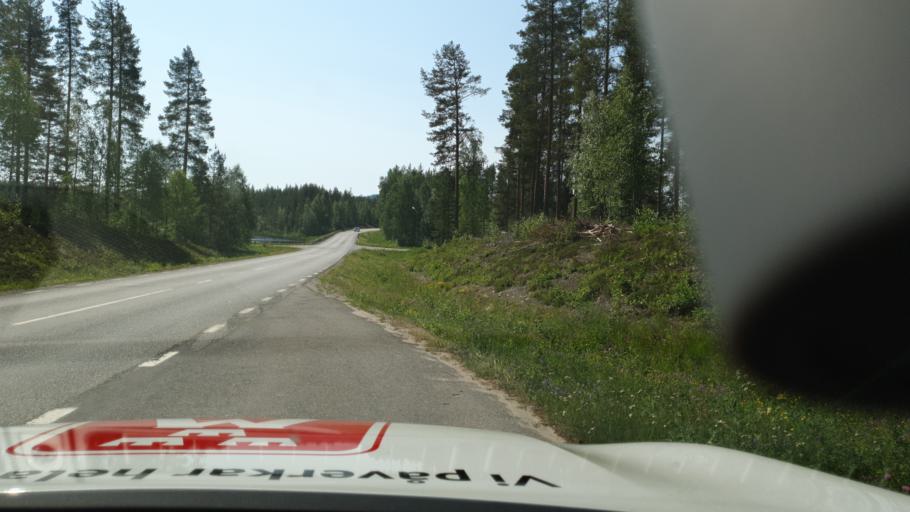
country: SE
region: Vaesterbotten
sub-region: Norsjo Kommun
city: Norsjoe
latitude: 64.9721
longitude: 19.7164
